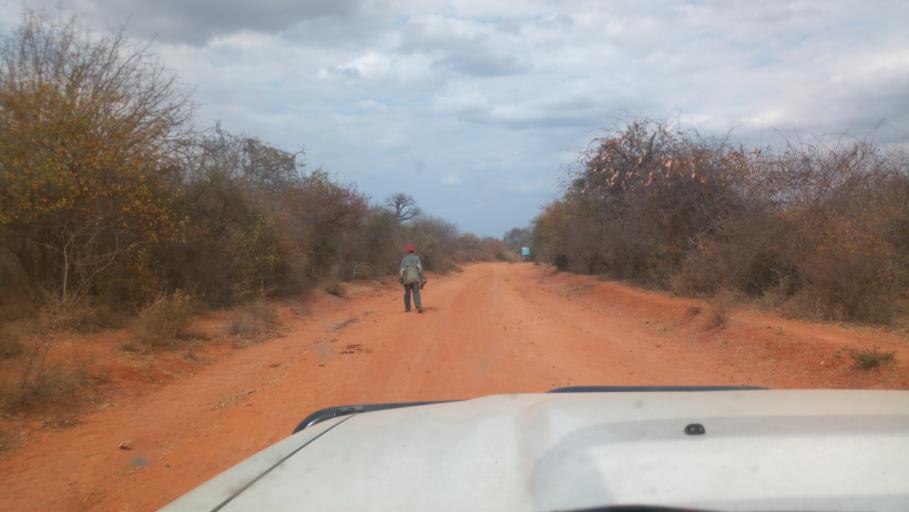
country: KE
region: Kitui
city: Kitui
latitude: -1.7993
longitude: 38.4535
